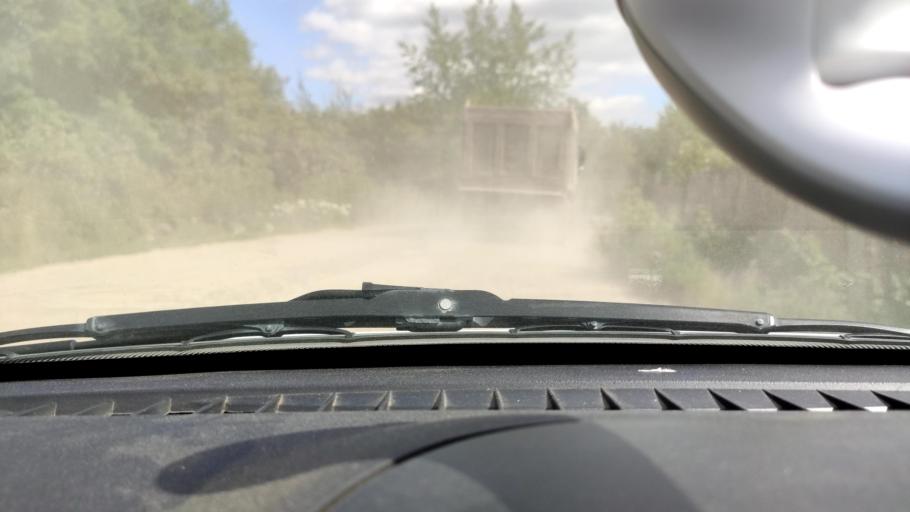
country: RU
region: Perm
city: Kondratovo
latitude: 58.0289
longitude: 56.0675
